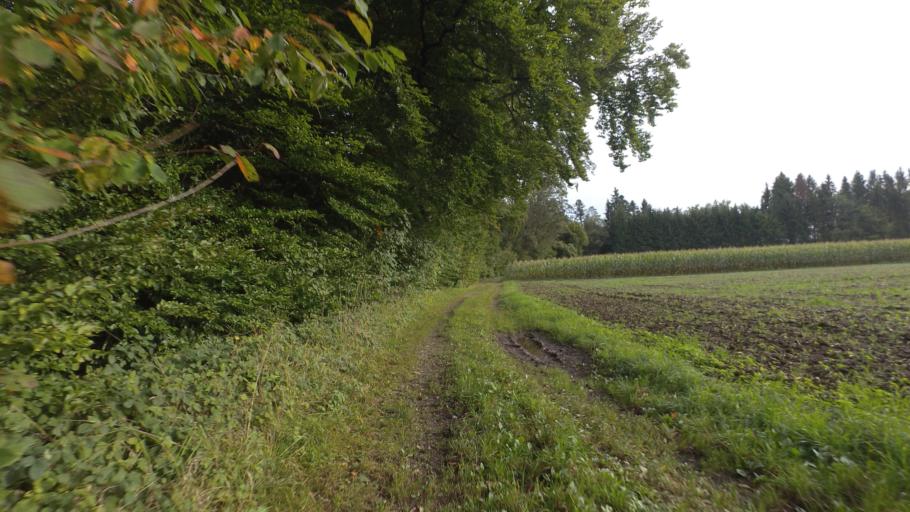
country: DE
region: Bavaria
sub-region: Upper Bavaria
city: Chieming
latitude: 47.9196
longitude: 12.5439
